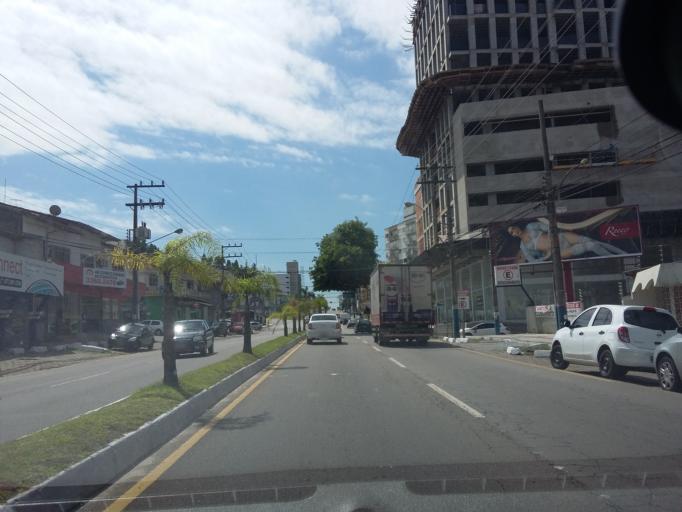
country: BR
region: Santa Catarina
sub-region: Balneario Camboriu
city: Balneario Camboriu
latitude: -26.9697
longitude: -48.6392
